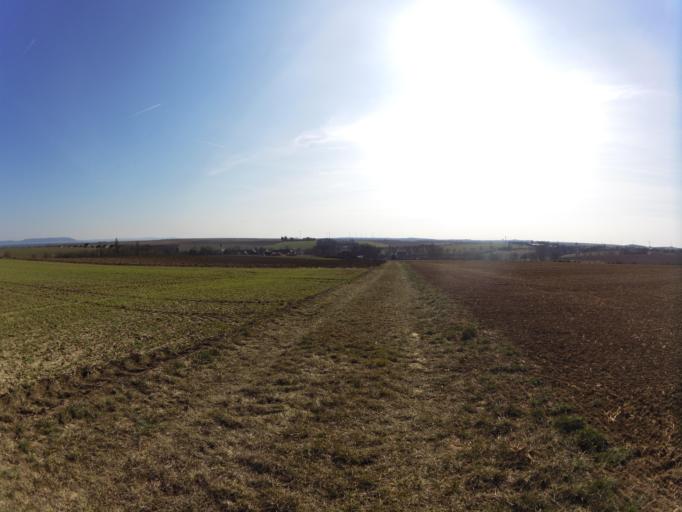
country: DE
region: Bavaria
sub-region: Regierungsbezirk Unterfranken
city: Prosselsheim
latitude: 49.8298
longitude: 10.1233
